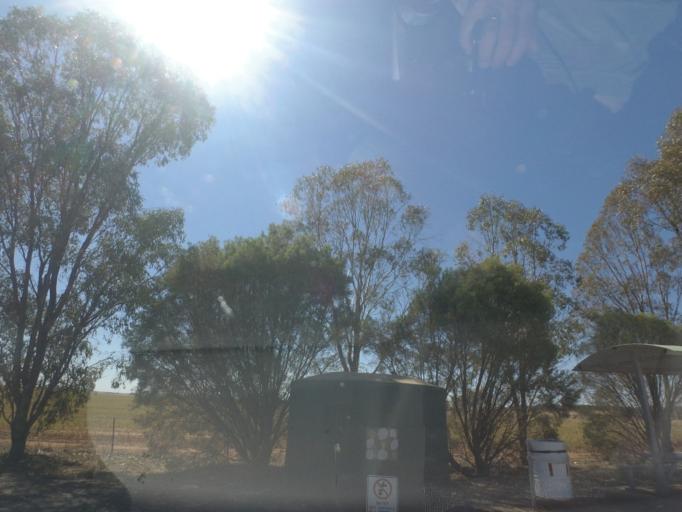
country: AU
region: New South Wales
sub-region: Narrandera
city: Narrandera
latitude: -34.4468
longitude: 146.8396
